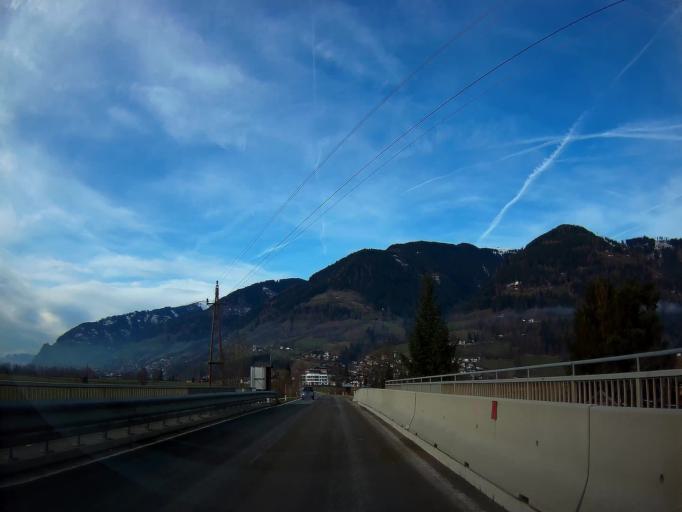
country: AT
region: Salzburg
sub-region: Politischer Bezirk Zell am See
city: Kaprun
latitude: 47.2842
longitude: 12.7520
